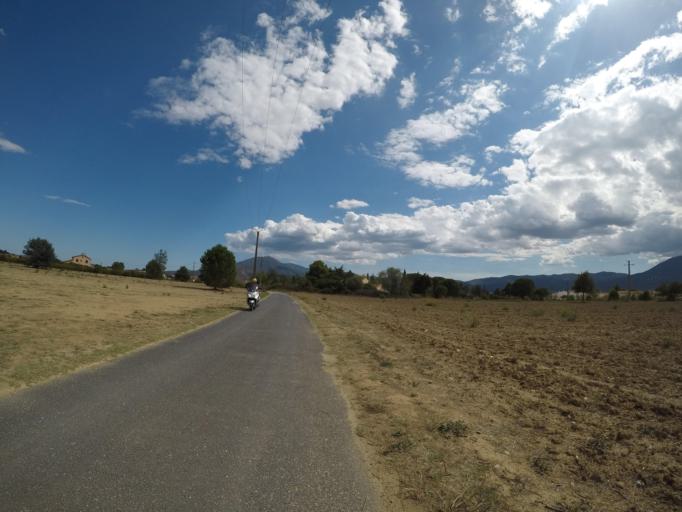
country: FR
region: Languedoc-Roussillon
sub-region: Departement des Pyrenees-Orientales
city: Sant Joan de Pladecorts
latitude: 42.5142
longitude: 2.7804
